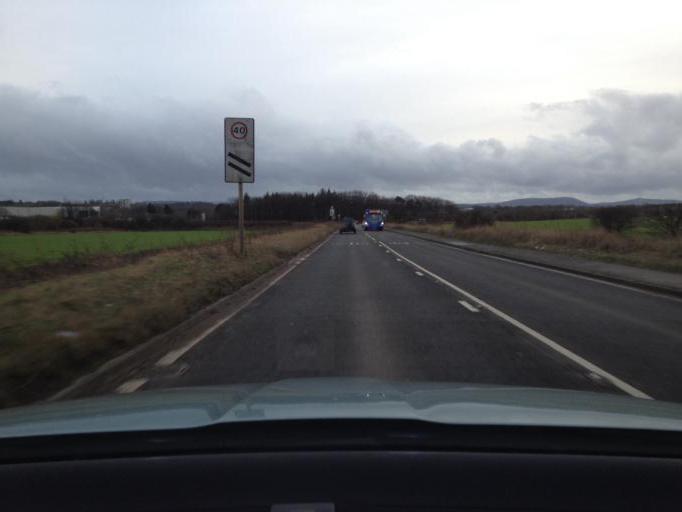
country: GB
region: Scotland
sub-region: Edinburgh
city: Kirkliston
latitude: 55.9438
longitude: -3.4138
